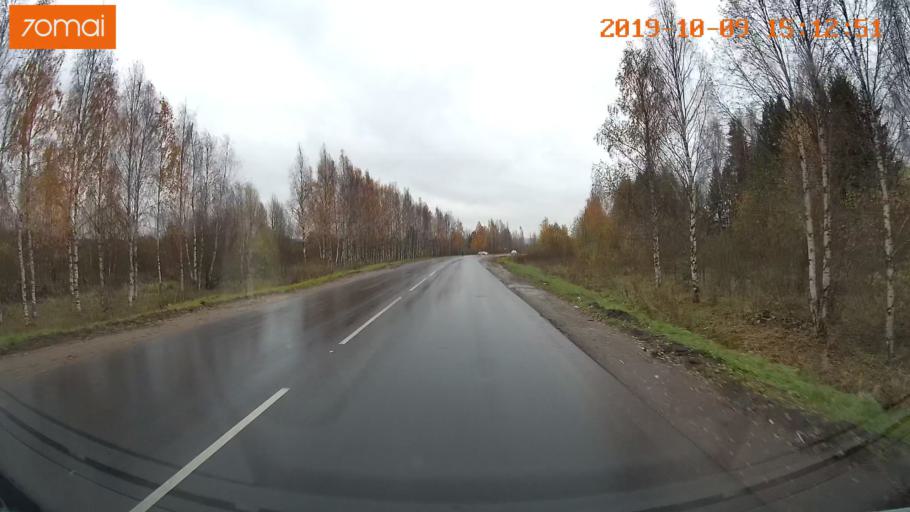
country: RU
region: Kostroma
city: Susanino
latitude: 58.1537
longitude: 41.6122
